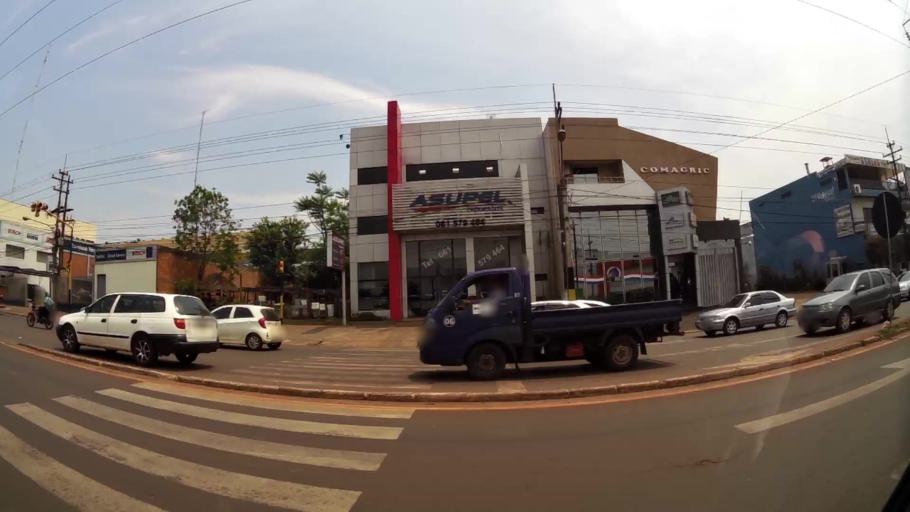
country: PY
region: Alto Parana
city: Ciudad del Este
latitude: -25.4977
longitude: -54.6347
